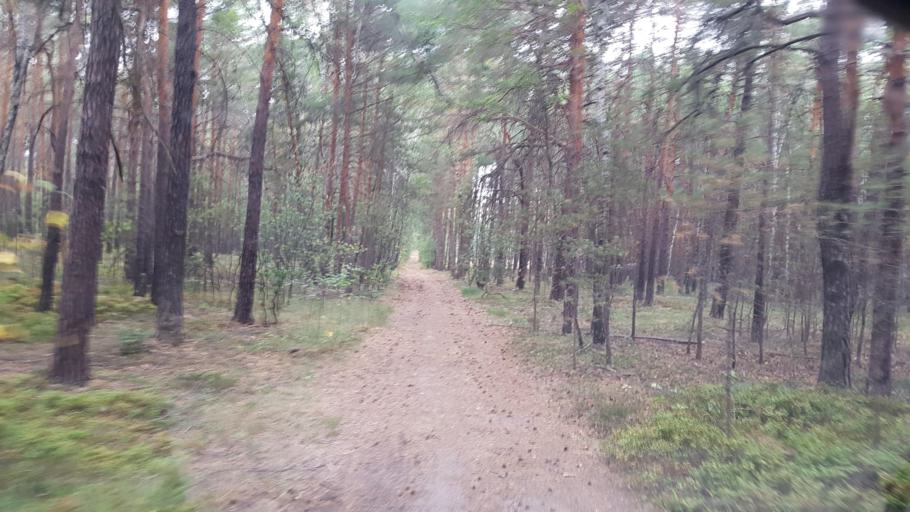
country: DE
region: Brandenburg
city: Sallgast
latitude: 51.6033
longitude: 13.8287
